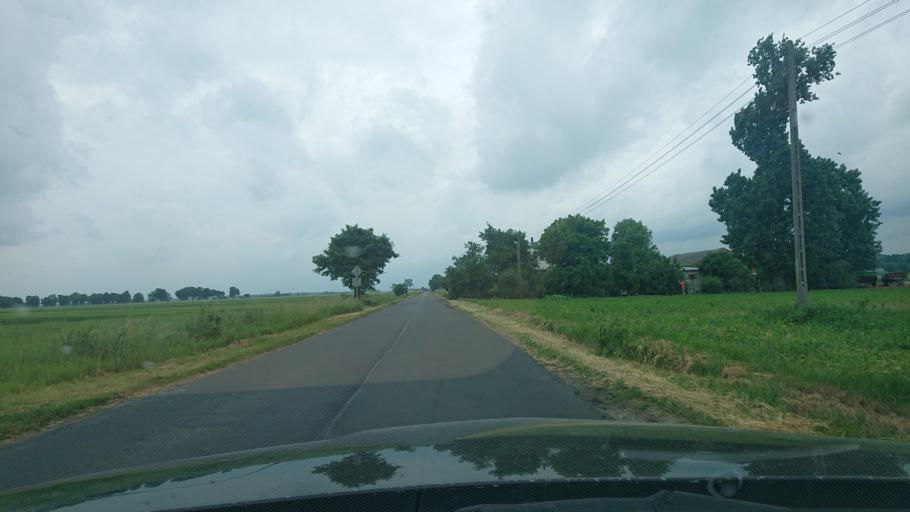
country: PL
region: Greater Poland Voivodeship
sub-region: Powiat gnieznienski
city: Czerniejewo
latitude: 52.4500
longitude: 17.5489
